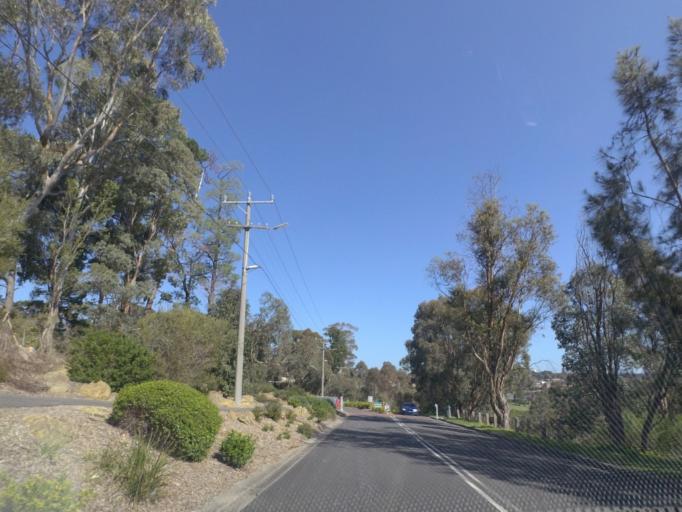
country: AU
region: Victoria
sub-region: Manningham
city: Doncaster East
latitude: -37.7748
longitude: 145.1401
